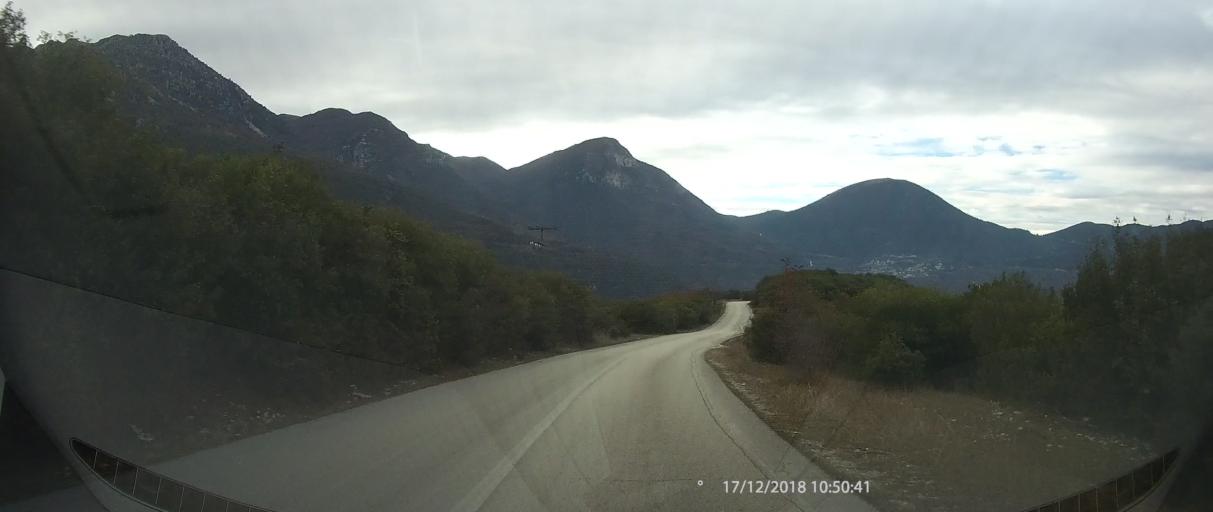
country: GR
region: Epirus
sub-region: Nomos Ioanninon
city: Kalpaki
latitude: 39.9551
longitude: 20.6958
